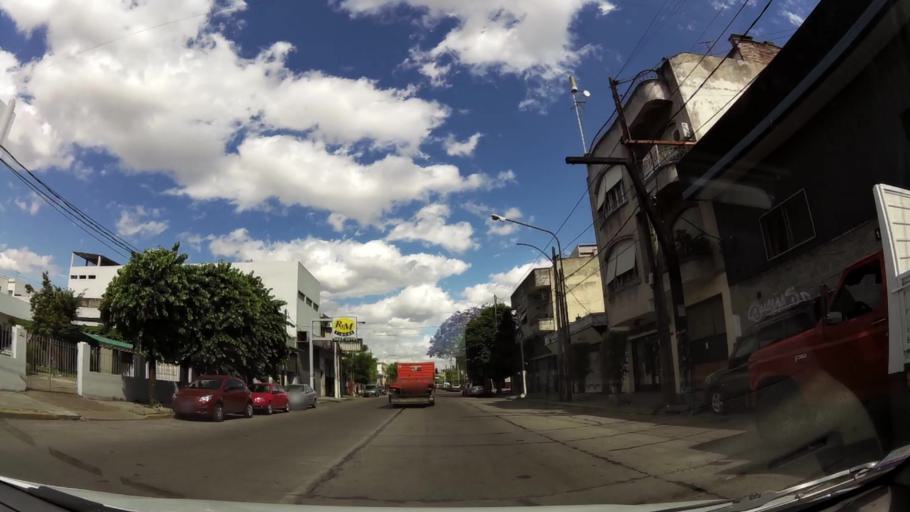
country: AR
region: Buenos Aires
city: San Justo
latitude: -34.6476
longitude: -58.5388
